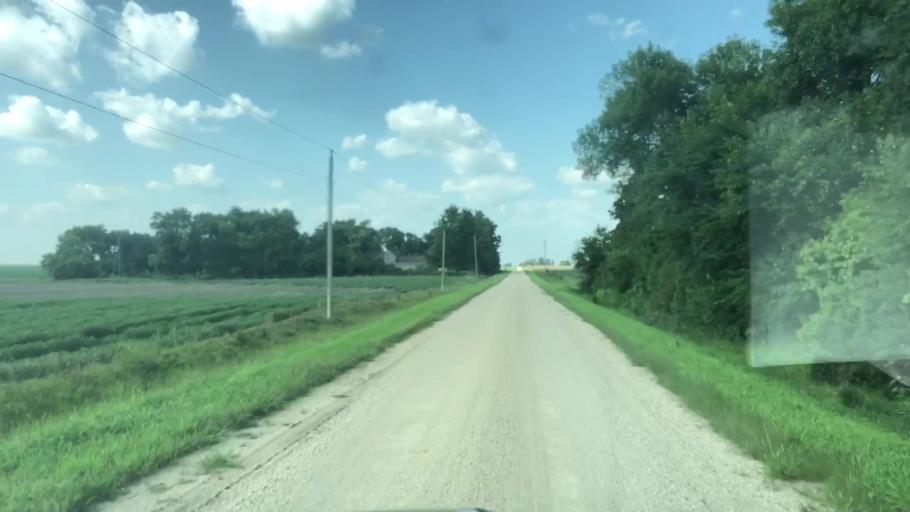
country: US
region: Iowa
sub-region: O'Brien County
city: Sheldon
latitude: 43.1730
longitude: -95.7823
